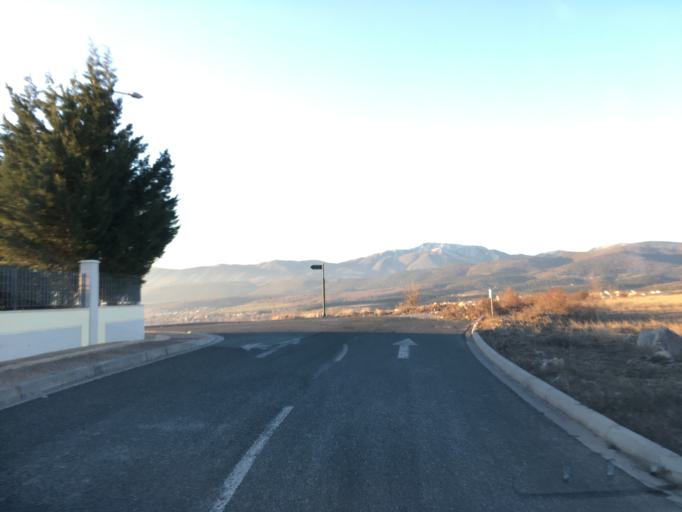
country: GR
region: West Macedonia
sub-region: Nomos Kozanis
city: Kozani
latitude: 40.2711
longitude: 21.7564
